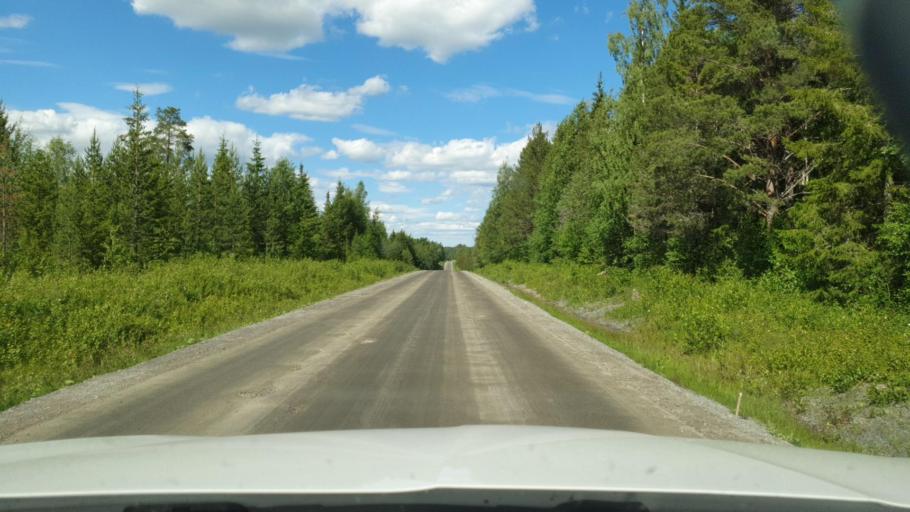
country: SE
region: Vaesterbotten
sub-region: Skelleftea Kommun
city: Forsbacka
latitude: 64.7764
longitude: 20.5160
